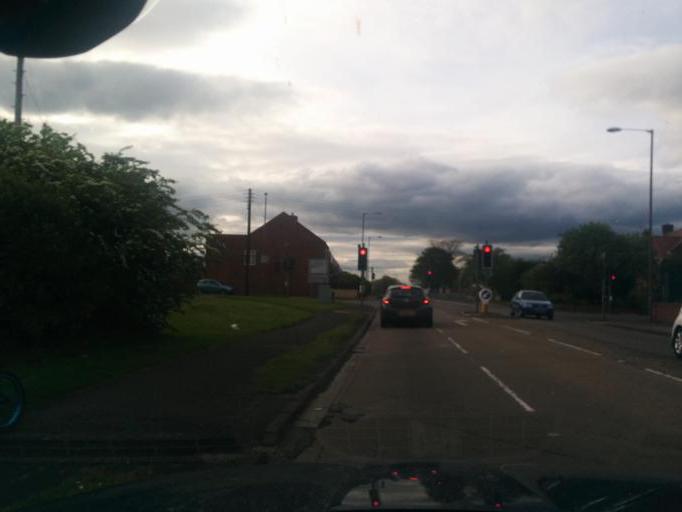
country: GB
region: England
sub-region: Northumberland
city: Bedlington
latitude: 55.1408
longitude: -1.5616
